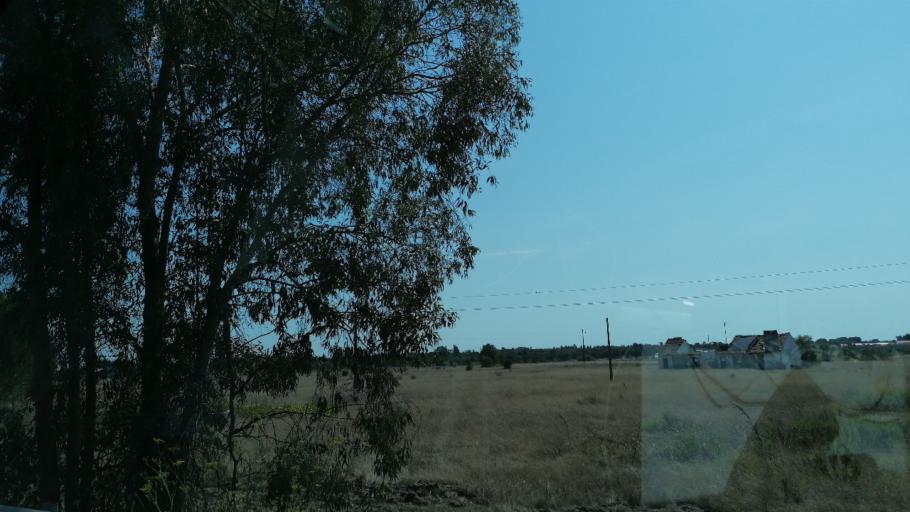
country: PT
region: Santarem
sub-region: Benavente
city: Poceirao
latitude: 38.7381
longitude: -8.6554
